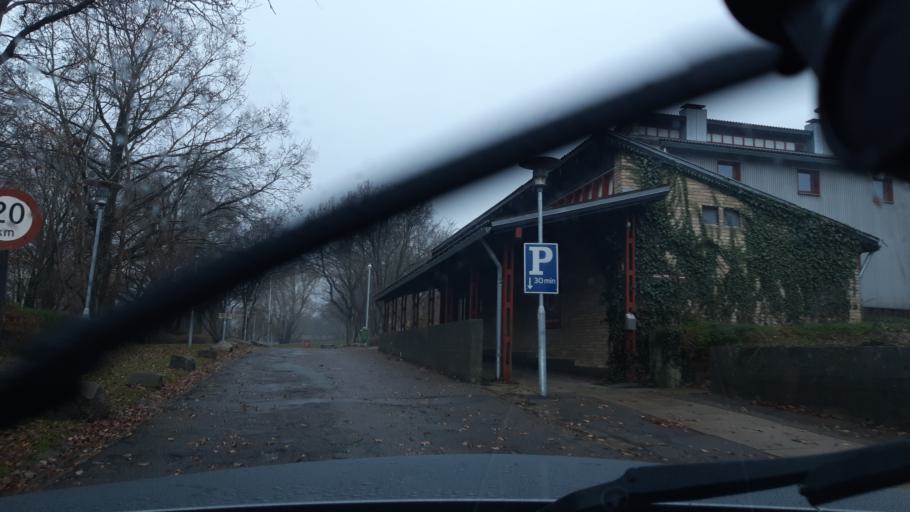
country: DK
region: Capital Region
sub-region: Herlev Kommune
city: Herlev
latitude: 55.7602
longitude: 12.4470
